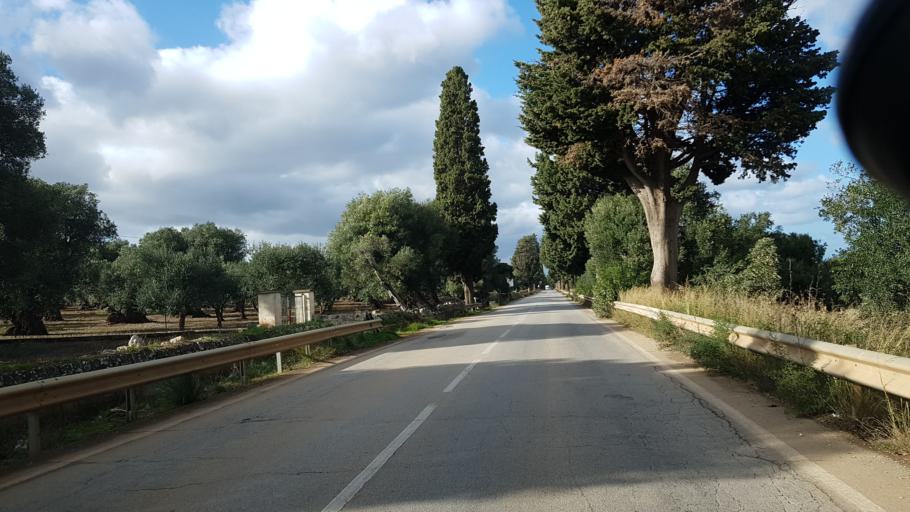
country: IT
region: Apulia
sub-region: Provincia di Brindisi
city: Ostuni
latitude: 40.7504
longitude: 17.5514
